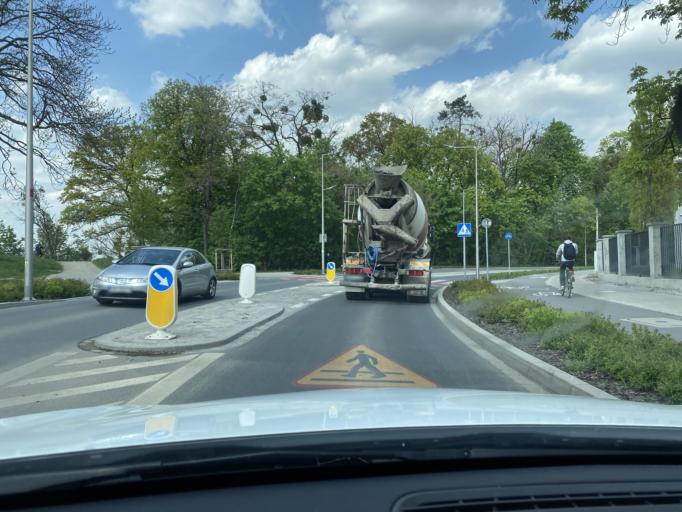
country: PL
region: Lower Silesian Voivodeship
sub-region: Powiat wroclawski
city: Wroclaw
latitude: 51.1390
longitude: 16.9909
